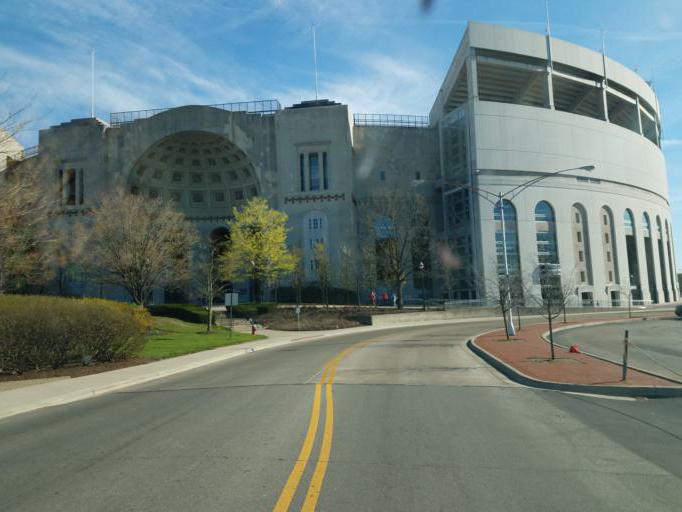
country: US
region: Ohio
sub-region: Franklin County
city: Grandview Heights
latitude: 40.0036
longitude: -83.0198
